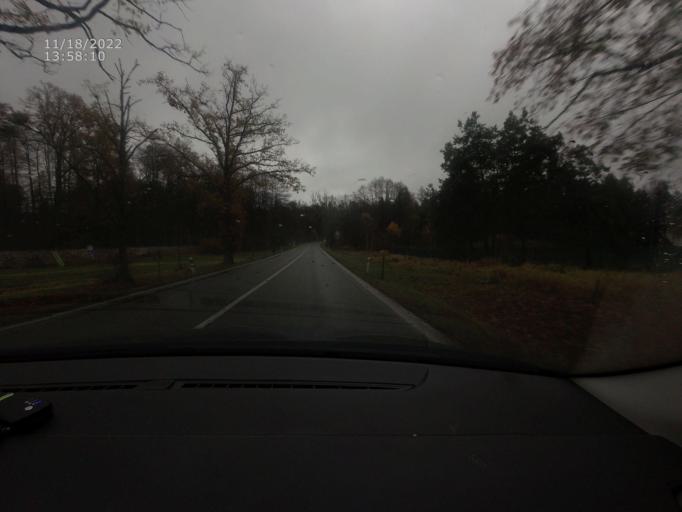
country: CZ
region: Jihocesky
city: Sedlice
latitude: 49.3648
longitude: 13.9773
